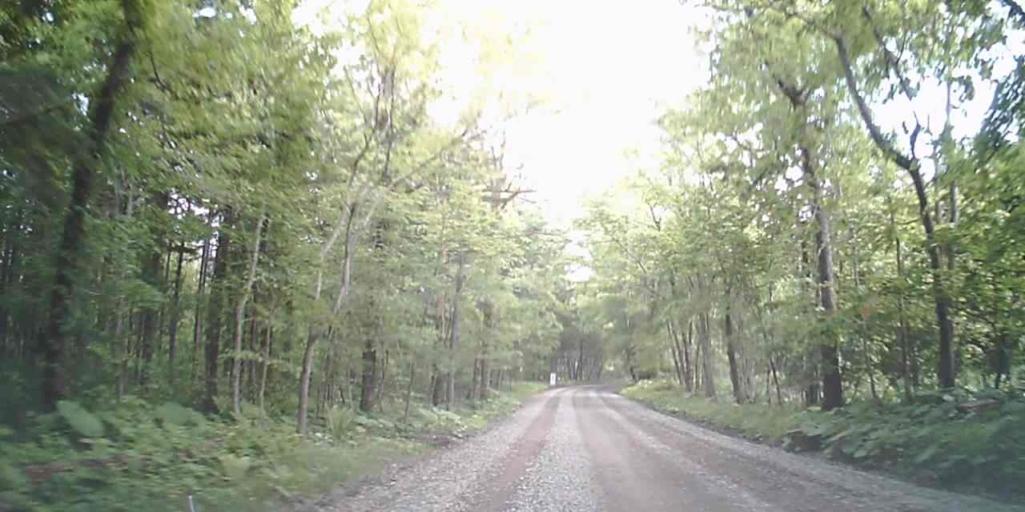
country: JP
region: Hokkaido
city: Tomakomai
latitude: 42.7560
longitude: 141.4282
